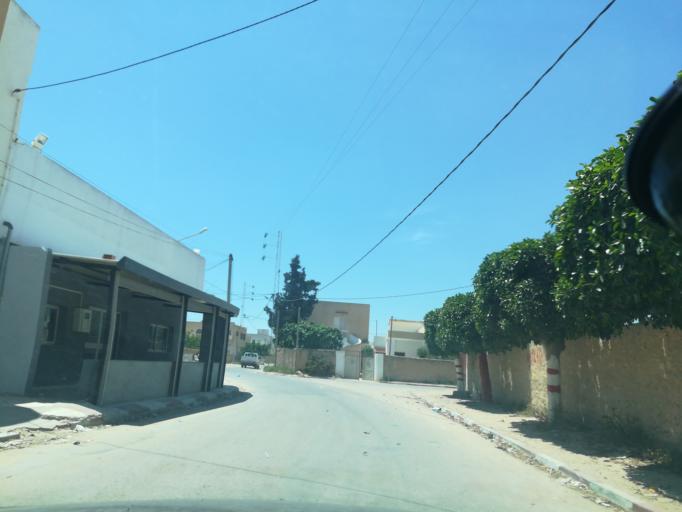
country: TN
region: Safaqis
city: Al Qarmadah
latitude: 34.8180
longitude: 10.7592
